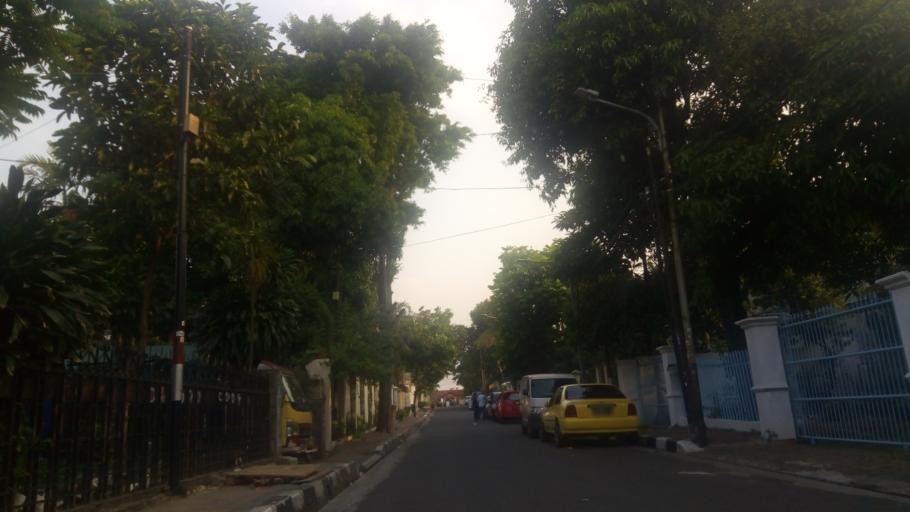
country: ID
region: Jakarta Raya
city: Jakarta
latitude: -6.2040
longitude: 106.8515
